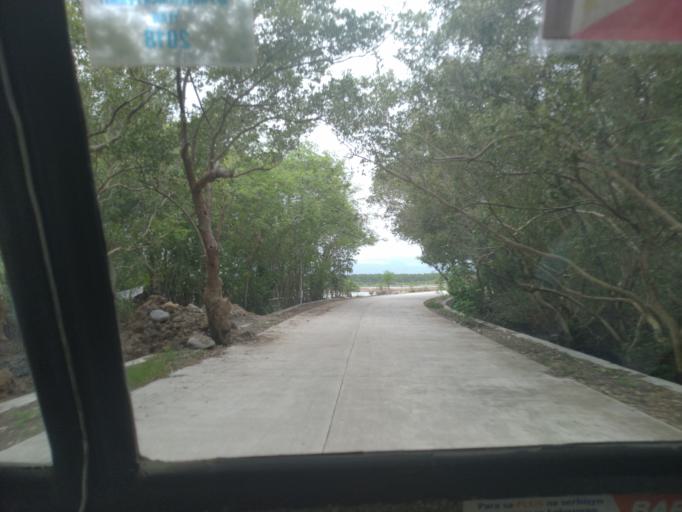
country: PH
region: Central Visayas
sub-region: Province of Negros Oriental
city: Tanjay
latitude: 9.5412
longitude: 123.1545
